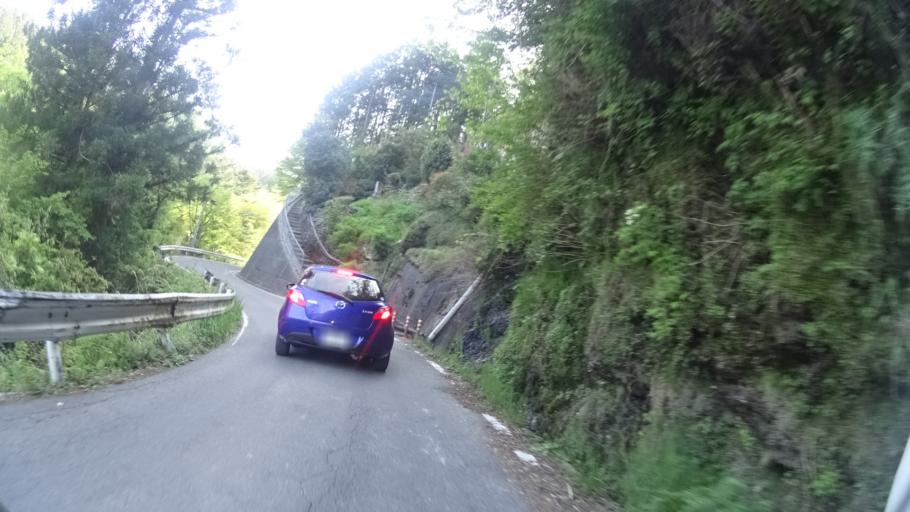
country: JP
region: Tokushima
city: Ikedacho
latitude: 33.8741
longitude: 133.9870
